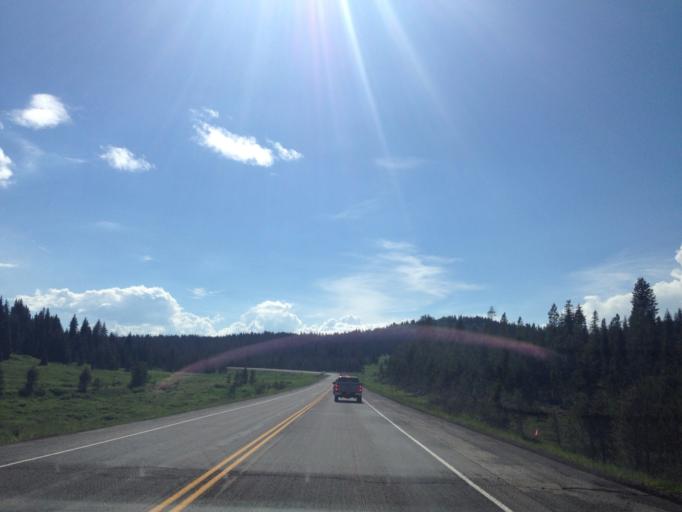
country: US
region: Colorado
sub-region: Routt County
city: Steamboat Springs
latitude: 40.3759
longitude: -106.7275
